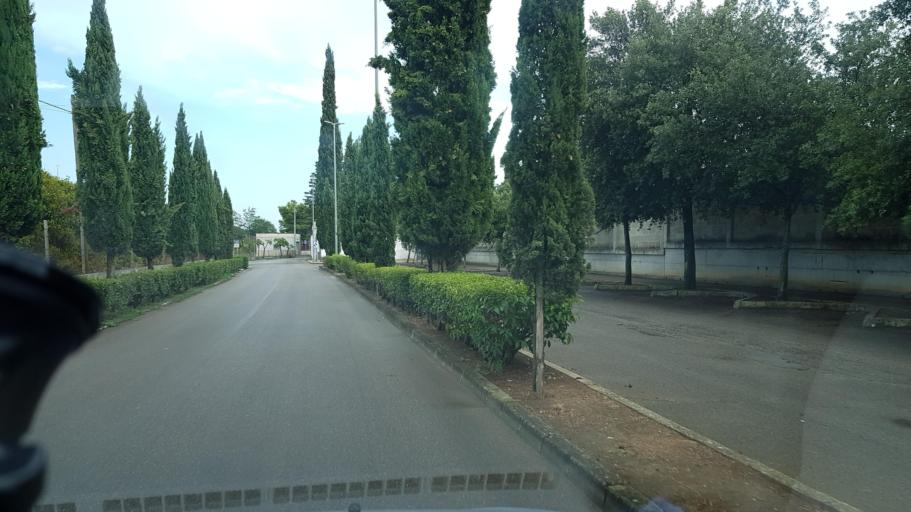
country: IT
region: Apulia
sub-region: Provincia di Brindisi
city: Oria
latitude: 40.5004
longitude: 17.6488
